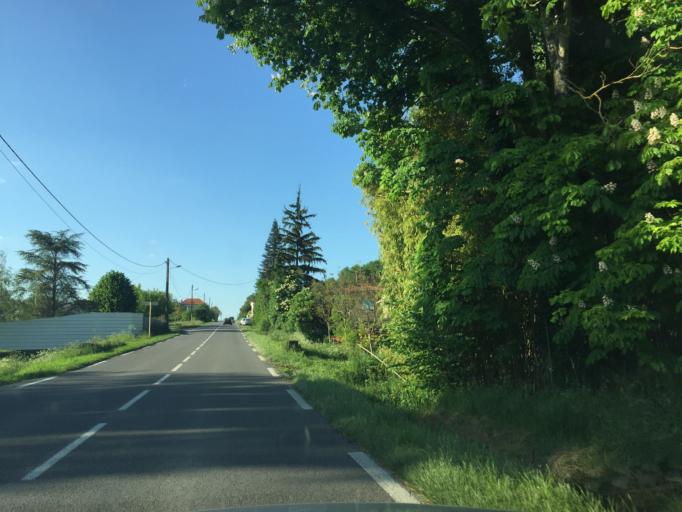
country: FR
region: Poitou-Charentes
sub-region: Departement de la Charente
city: Chalais
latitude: 45.2334
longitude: 0.0369
